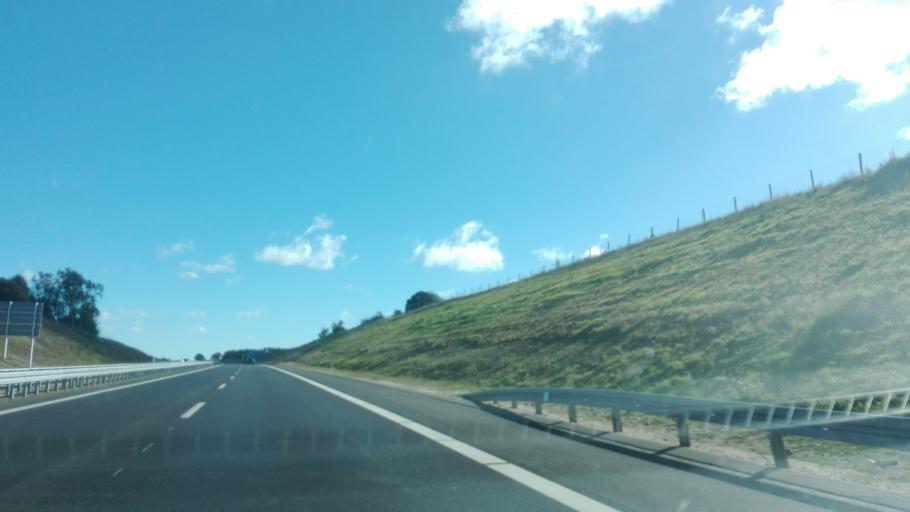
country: DK
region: Central Jutland
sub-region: Silkeborg Kommune
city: Svejbaek
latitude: 56.1569
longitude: 9.6223
